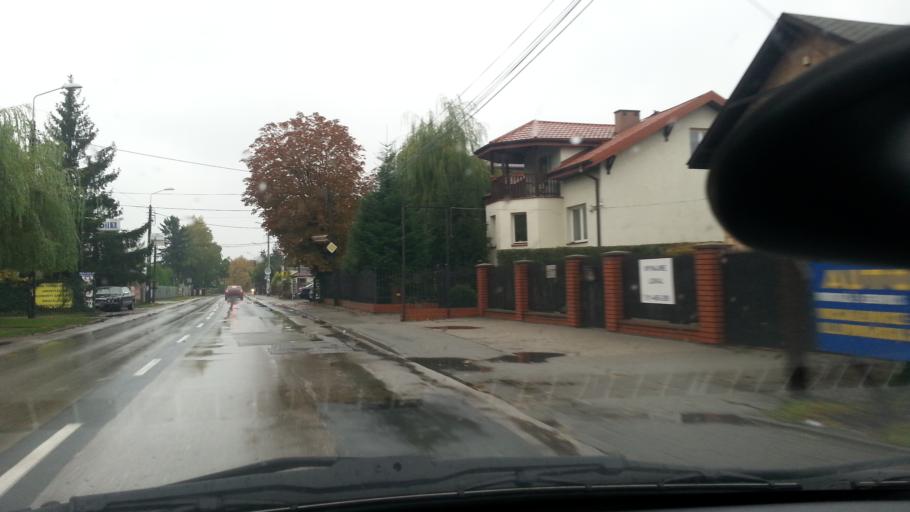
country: PL
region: Masovian Voivodeship
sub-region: Powiat pruszkowski
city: Michalowice
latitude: 52.1734
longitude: 20.8624
